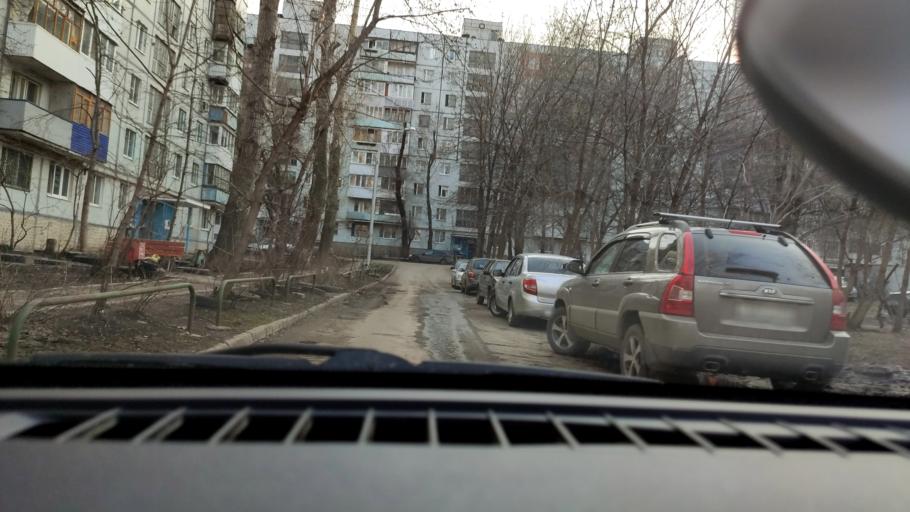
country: RU
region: Samara
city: Petra-Dubrava
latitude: 53.2456
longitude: 50.2663
